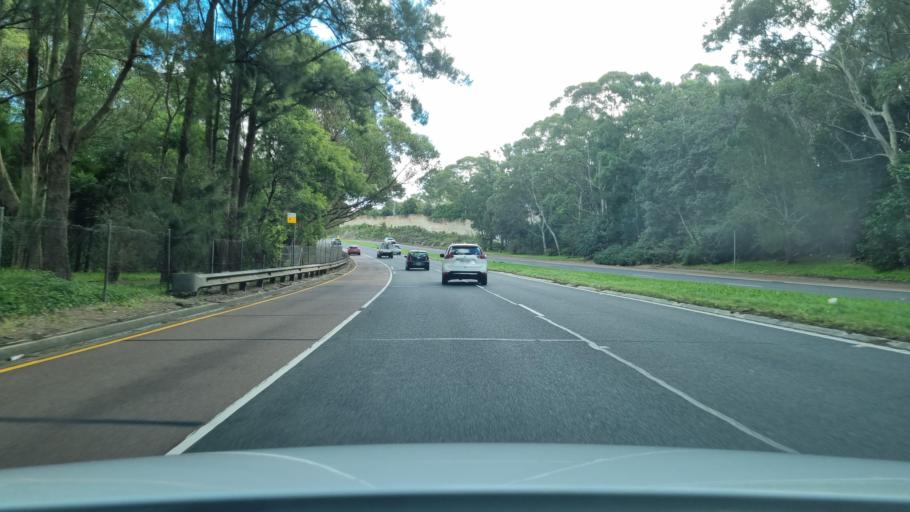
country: AU
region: New South Wales
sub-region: Manly Vale
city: Balgowlah
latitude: -33.7886
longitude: 151.2606
